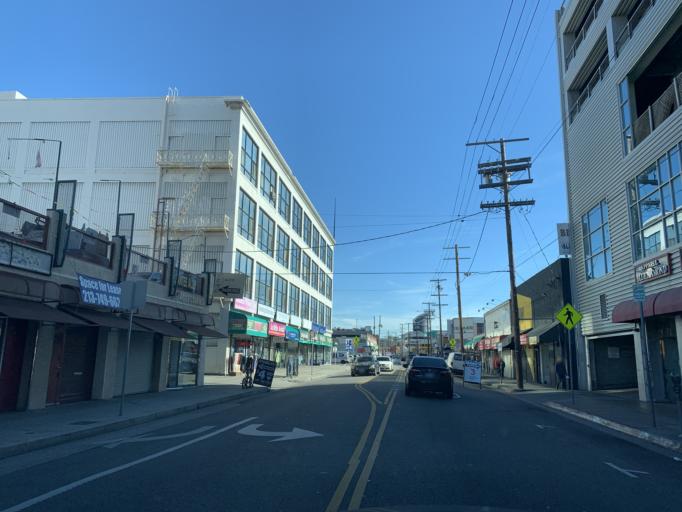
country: US
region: California
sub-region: Los Angeles County
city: Los Angeles
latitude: 34.0348
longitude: -118.2552
